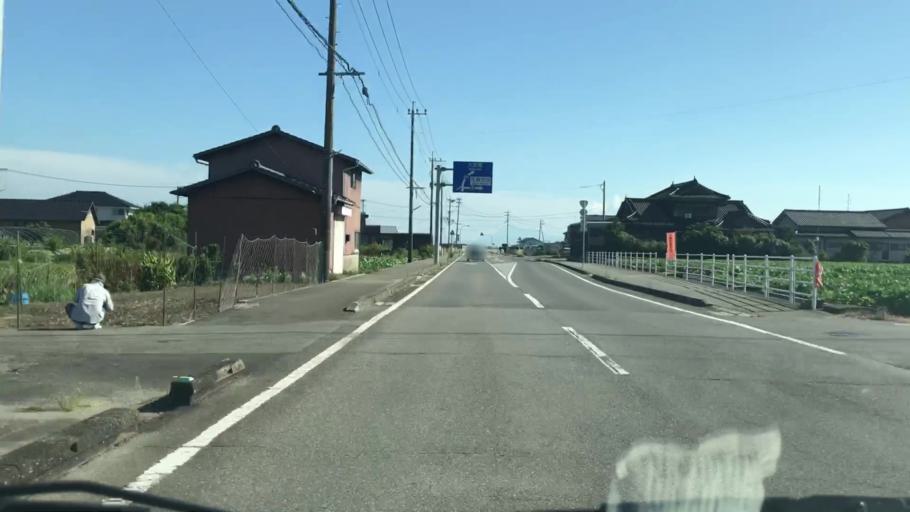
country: JP
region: Saga Prefecture
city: Okawa
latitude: 33.1988
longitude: 130.3351
